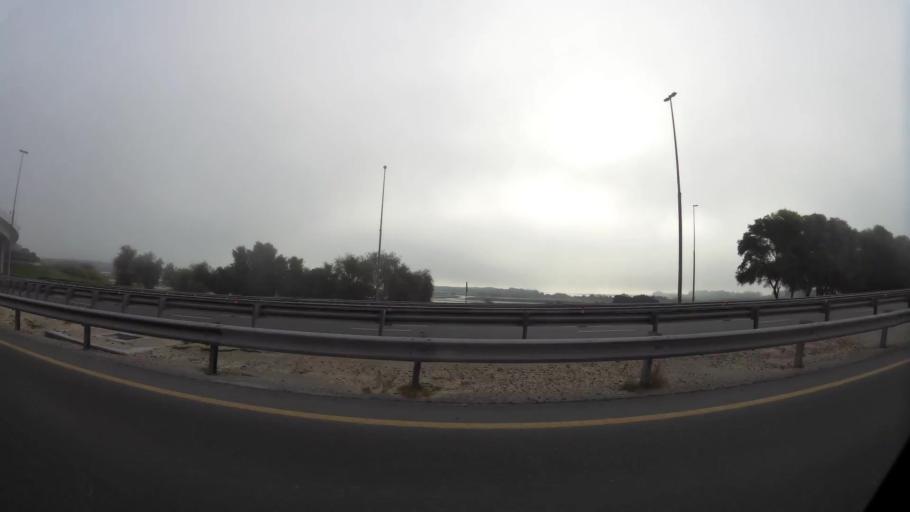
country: AE
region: Ash Shariqah
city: Sharjah
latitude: 25.1829
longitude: 55.3130
